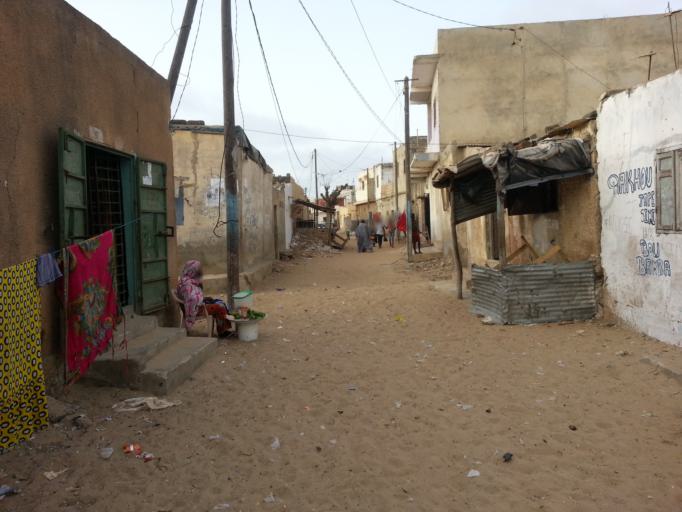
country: SN
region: Dakar
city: Pikine
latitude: 14.7696
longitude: -17.3860
